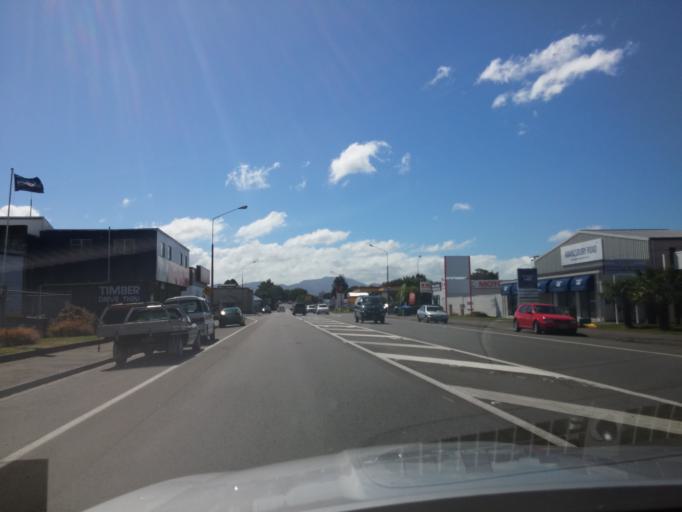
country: NZ
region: Marlborough
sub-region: Marlborough District
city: Blenheim
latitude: -41.5042
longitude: 173.9603
